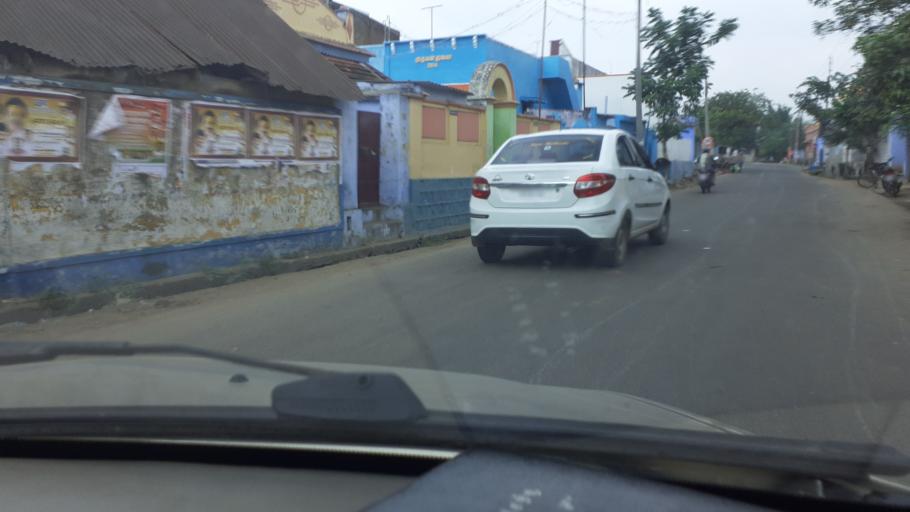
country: IN
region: Tamil Nadu
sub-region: Tirunelveli Kattabo
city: Viravanallur
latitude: 8.7201
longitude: 77.5462
